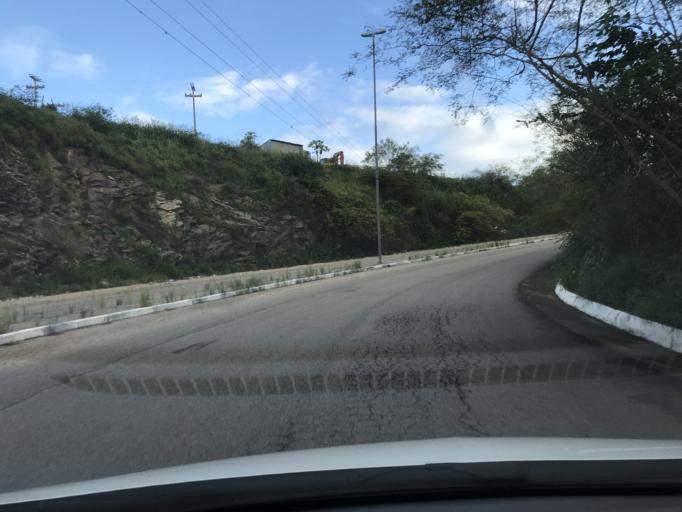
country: BR
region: Pernambuco
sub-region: Caruaru
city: Caruaru
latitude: -8.3081
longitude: -35.9424
